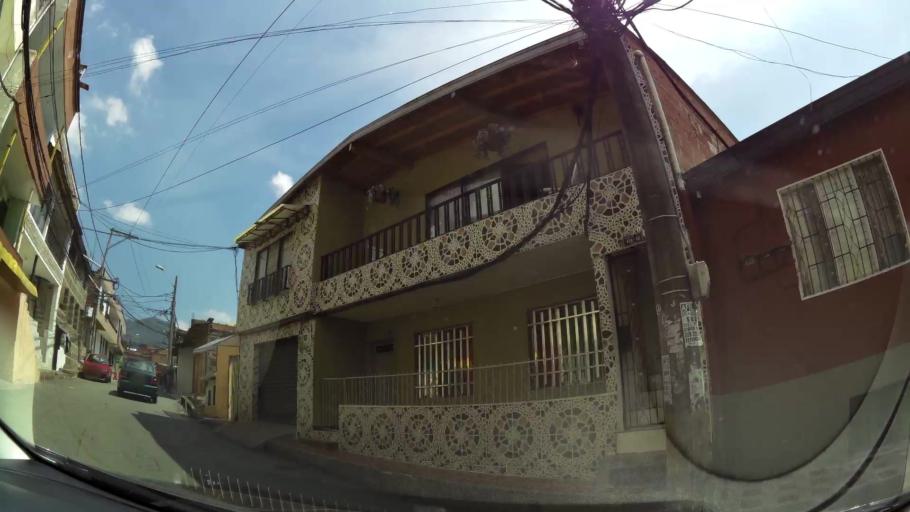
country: CO
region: Antioquia
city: La Estrella
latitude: 6.1843
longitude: -75.6595
